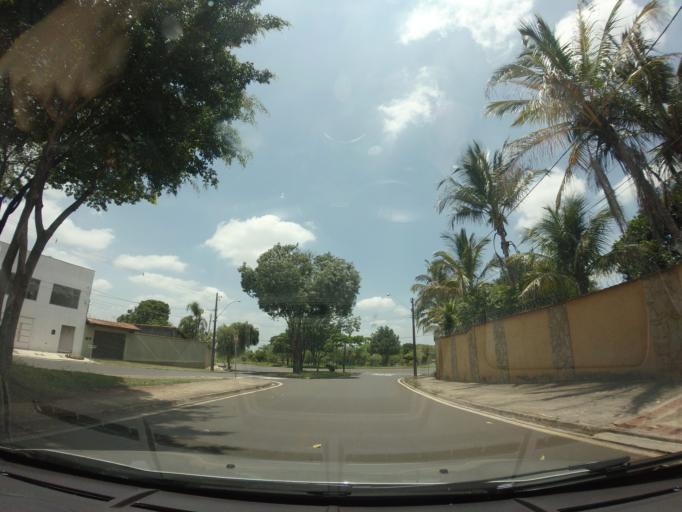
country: BR
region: Sao Paulo
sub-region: Piracicaba
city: Piracicaba
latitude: -22.7641
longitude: -47.5930
